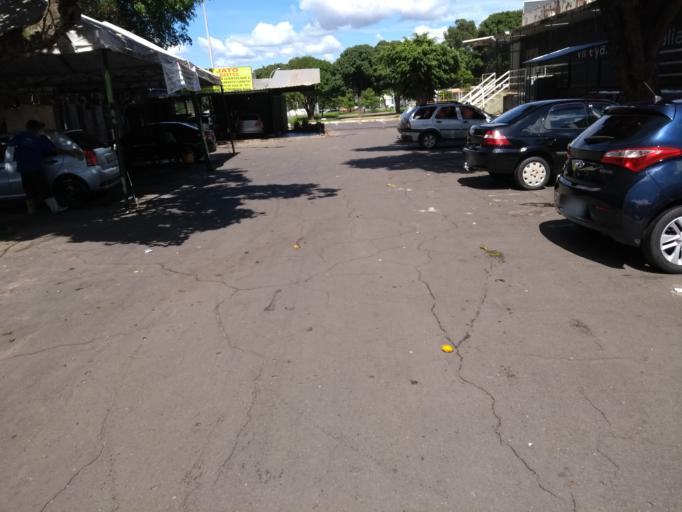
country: BR
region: Federal District
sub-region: Brasilia
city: Brasilia
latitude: -15.7926
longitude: -47.9403
